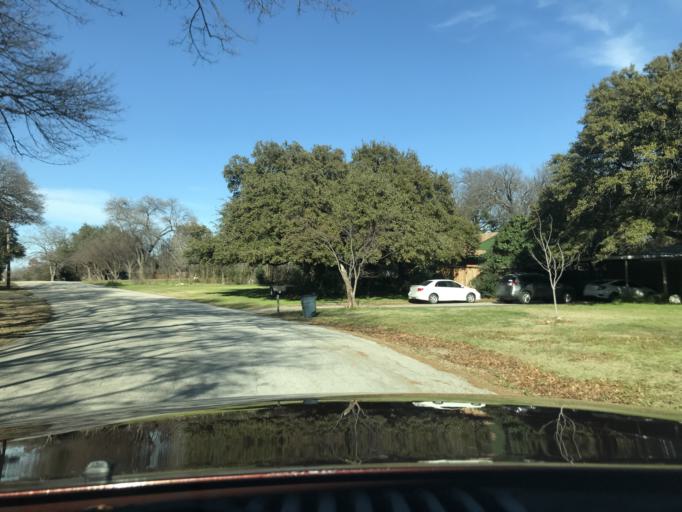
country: US
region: Texas
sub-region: Tarrant County
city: Edgecliff Village
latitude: 32.6594
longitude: -97.3433
